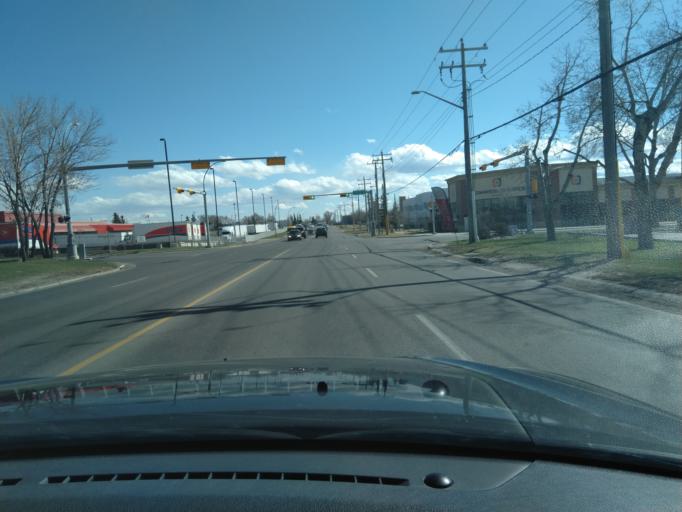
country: CA
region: Alberta
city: Calgary
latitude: 51.1005
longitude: -114.0365
